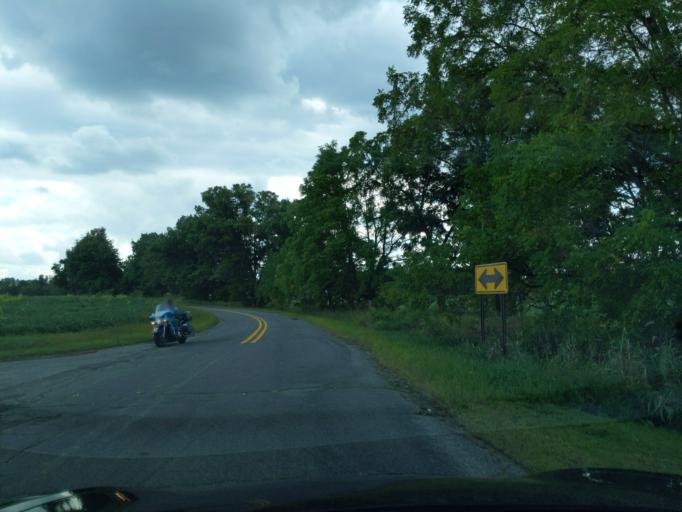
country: US
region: Michigan
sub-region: Eaton County
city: Eaton Rapids
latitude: 42.4221
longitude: -84.5805
